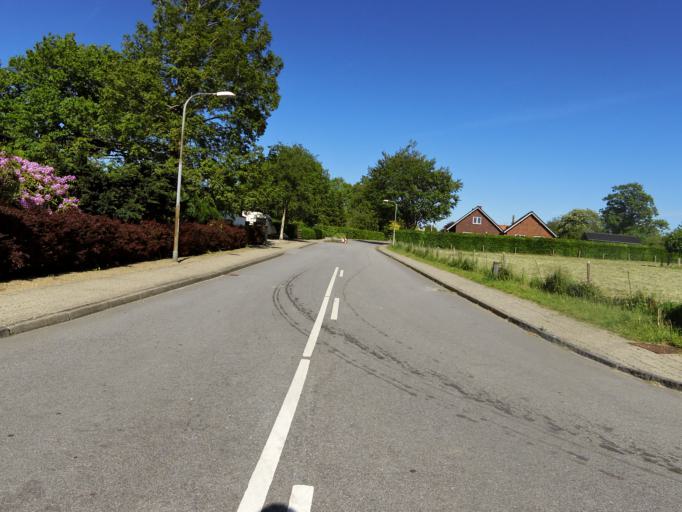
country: DK
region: South Denmark
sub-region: Haderslev Kommune
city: Gram
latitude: 55.2848
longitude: 9.0499
